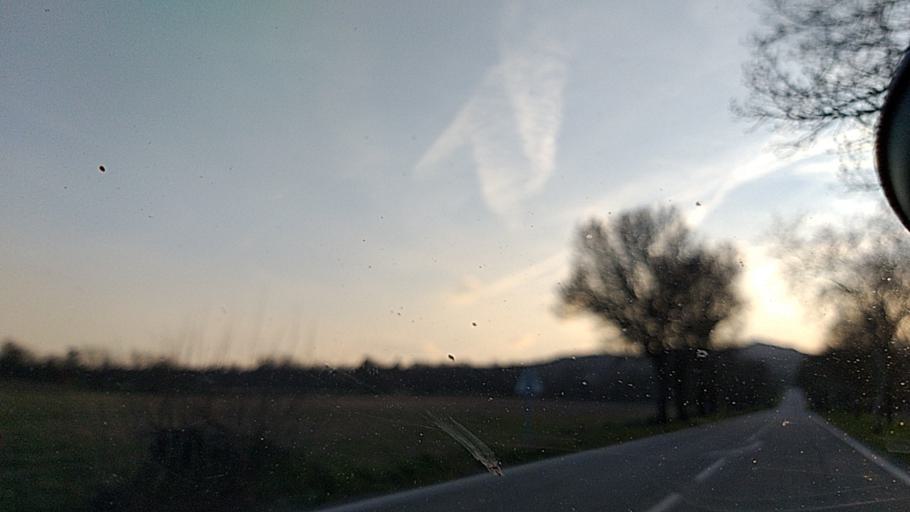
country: PT
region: Guarda
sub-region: Guarda
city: Sequeira
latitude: 40.5981
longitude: -7.1176
